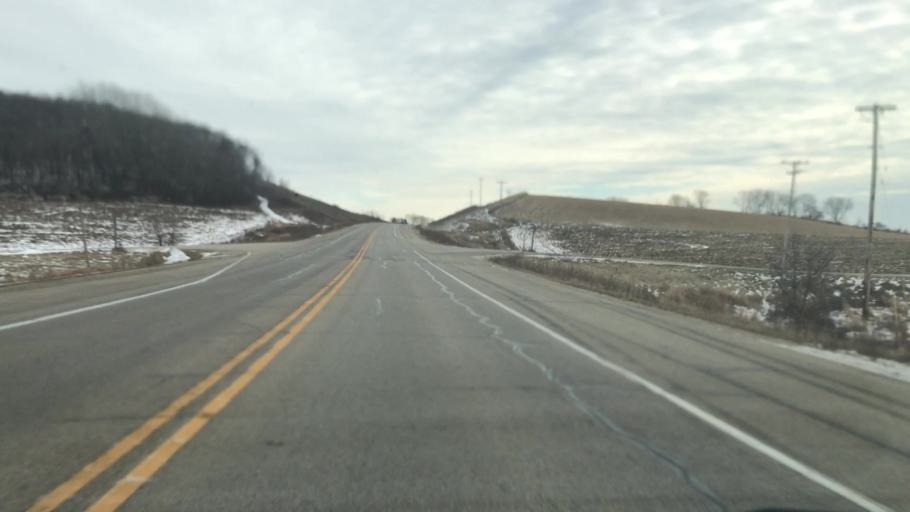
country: US
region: Wisconsin
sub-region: Dodge County
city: Theresa
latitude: 43.4336
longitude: -88.4609
